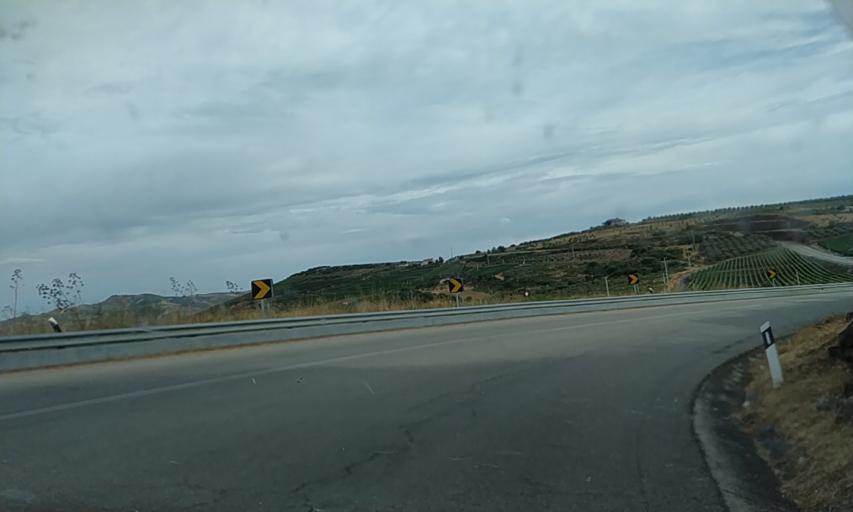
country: PT
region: Viseu
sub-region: Sao Joao da Pesqueira
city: Sao Joao da Pesqueira
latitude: 41.1348
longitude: -7.3980
